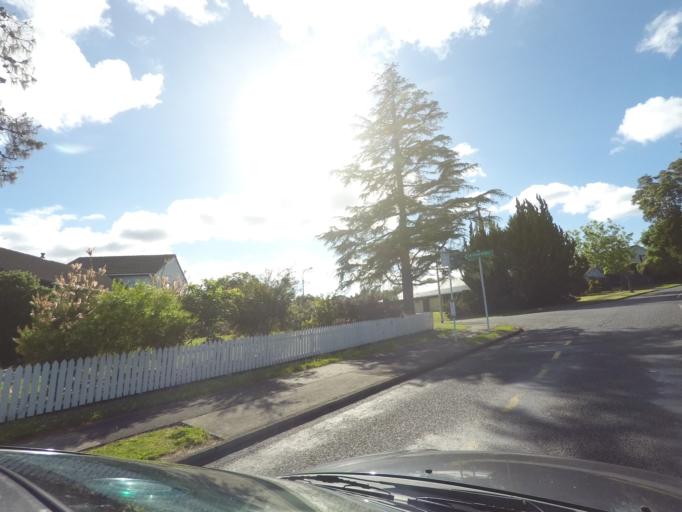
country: NZ
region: Auckland
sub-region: Auckland
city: Manukau City
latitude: -36.9894
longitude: 174.8911
